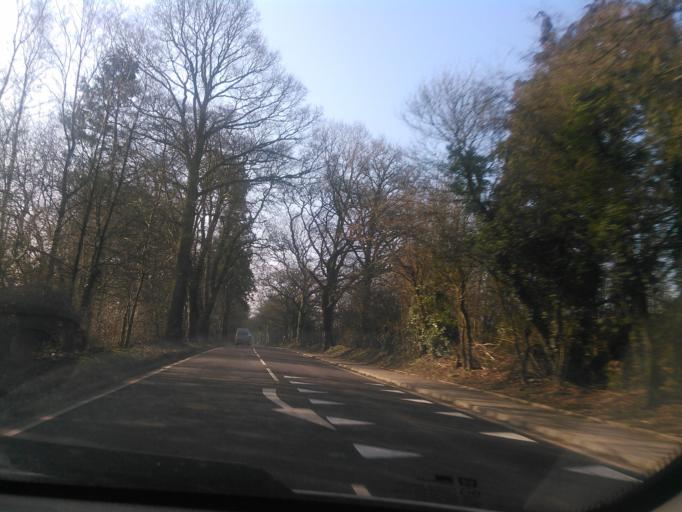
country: GB
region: England
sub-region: Shropshire
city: Craven Arms
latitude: 52.4548
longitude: -2.8373
